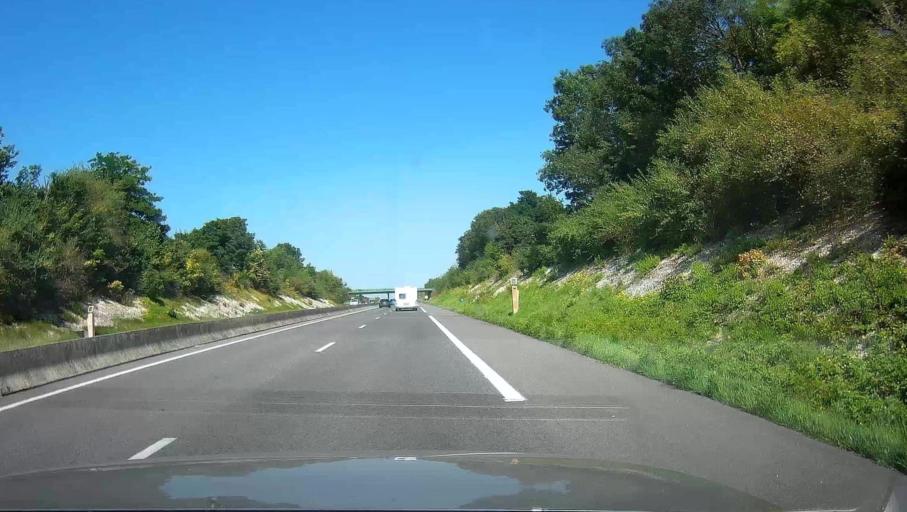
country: FR
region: Champagne-Ardenne
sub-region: Departement de l'Aube
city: Mailly-le-Camp
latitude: 48.6352
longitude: 4.1802
